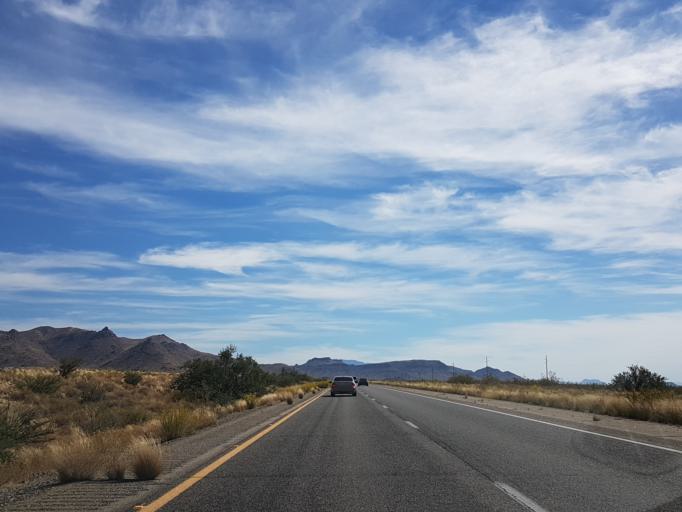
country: US
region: Arizona
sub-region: Mohave County
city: Golden Valley
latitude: 35.2752
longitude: -114.1715
